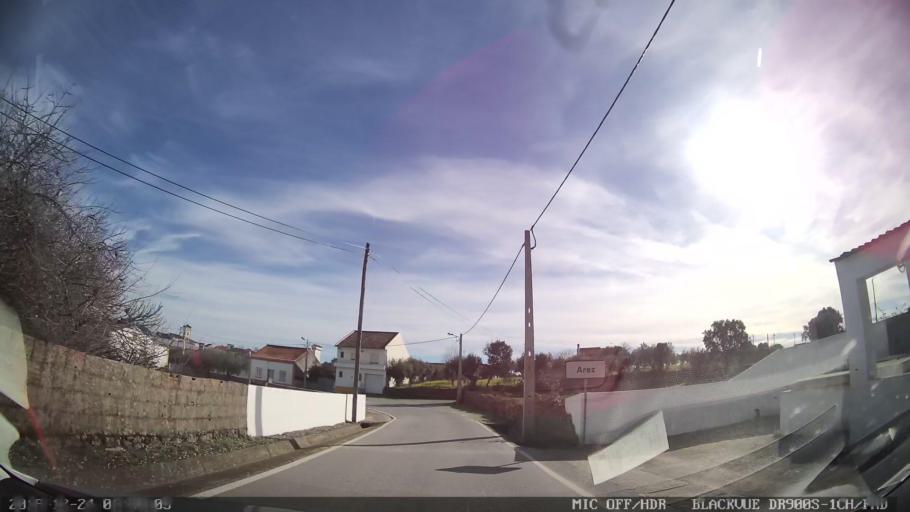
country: PT
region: Portalegre
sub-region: Nisa
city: Nisa
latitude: 39.4847
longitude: -7.7284
